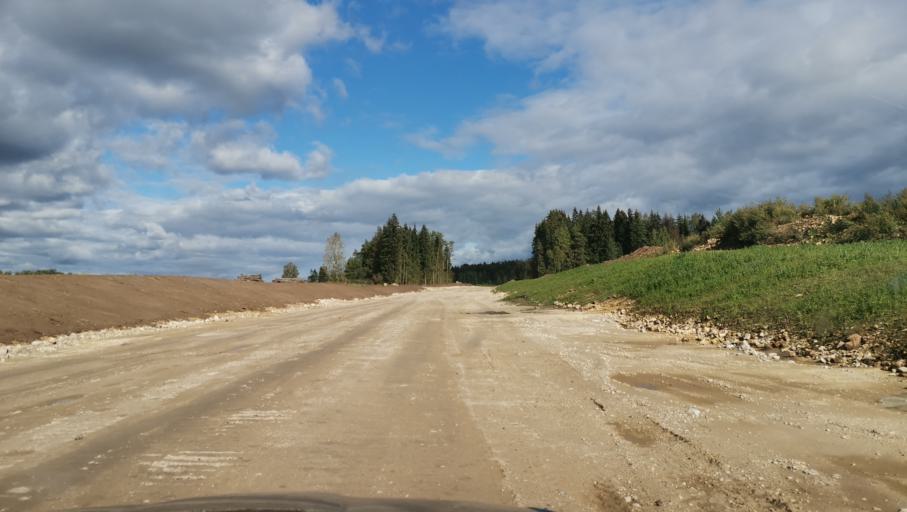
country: EE
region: Harju
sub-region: Nissi vald
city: Riisipere
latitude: 59.1341
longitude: 24.4819
